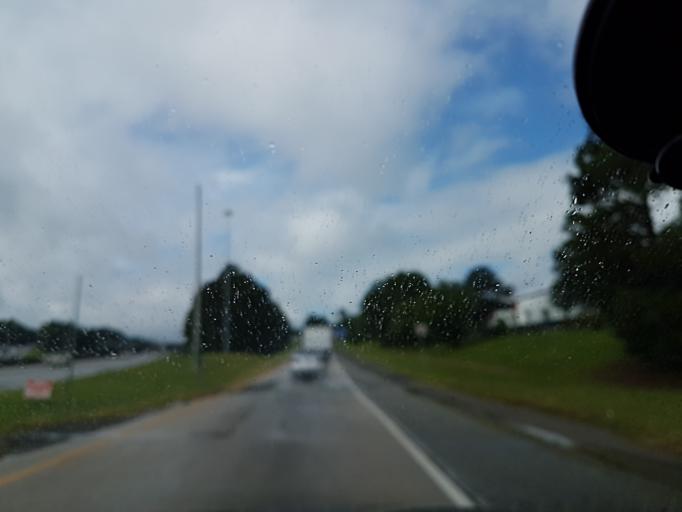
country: US
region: Georgia
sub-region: Fulton County
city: Union City
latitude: 33.5704
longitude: -84.5308
